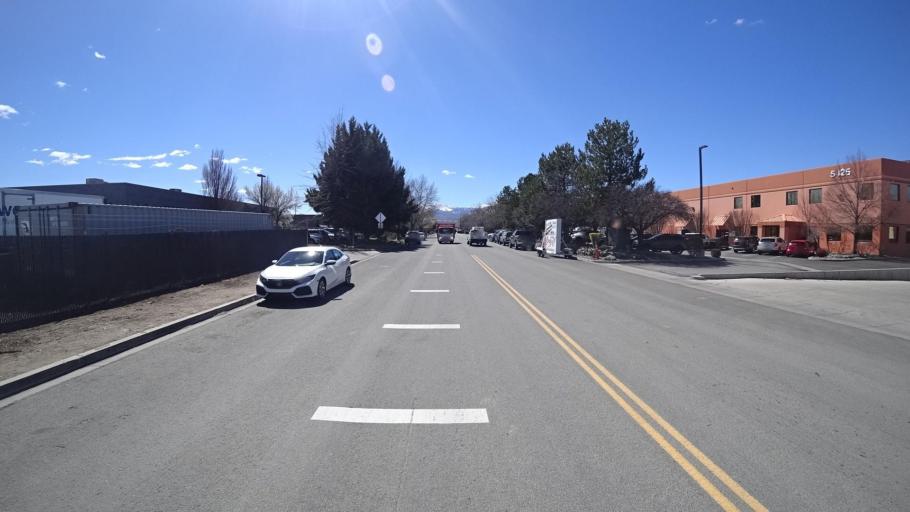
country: US
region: Nevada
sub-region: Washoe County
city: Sparks
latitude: 39.4718
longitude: -119.7699
